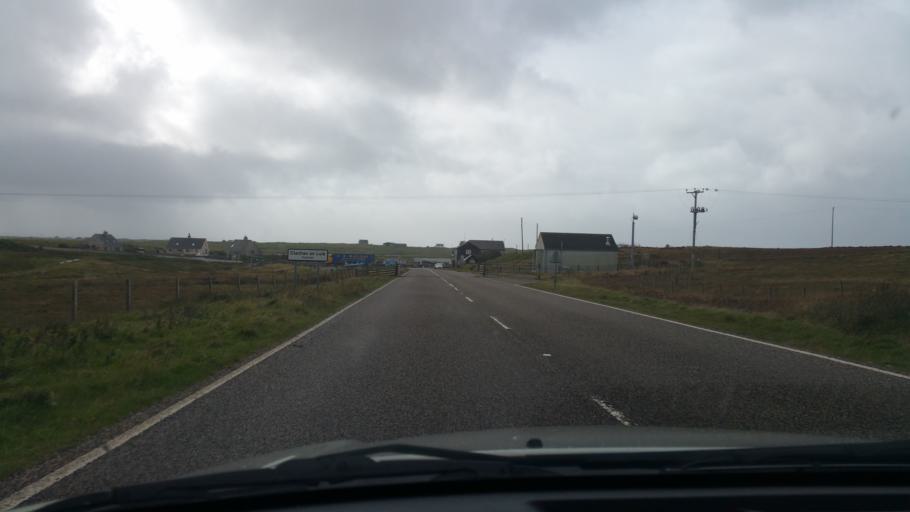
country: GB
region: Scotland
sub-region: Eilean Siar
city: Isle of North Uist
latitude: 57.5545
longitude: -7.3313
